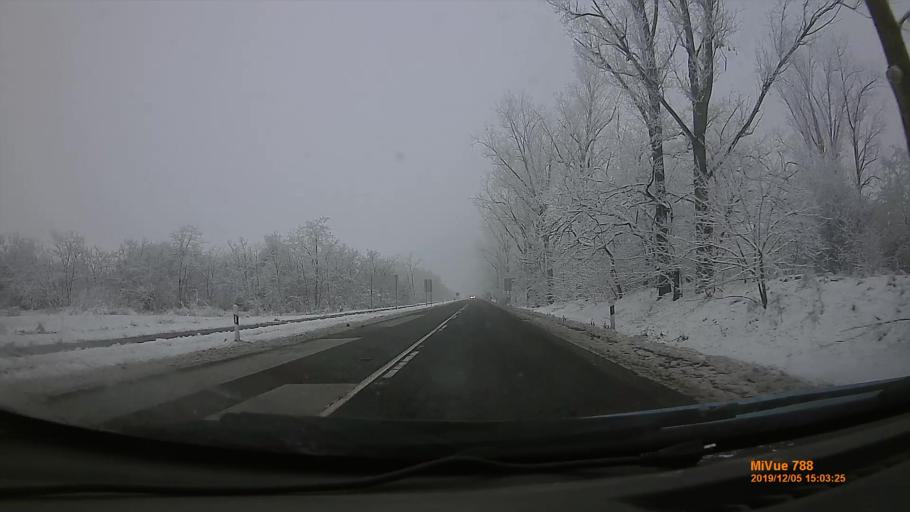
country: HU
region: Szabolcs-Szatmar-Bereg
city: Tiszanagyfalu
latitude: 48.0836
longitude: 21.4990
